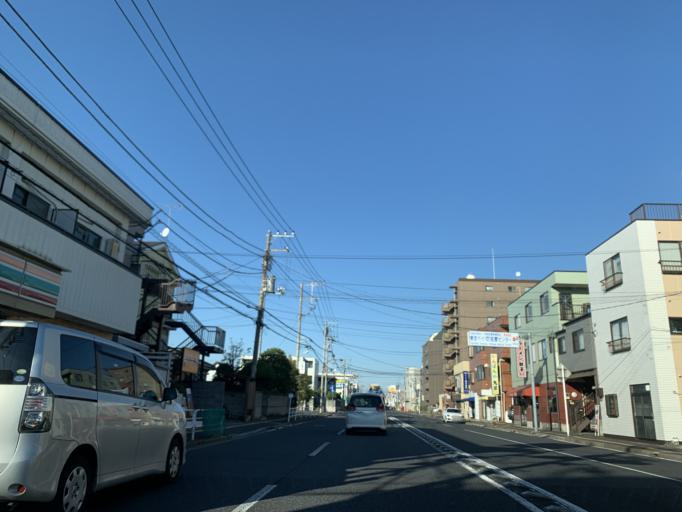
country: JP
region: Tokyo
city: Urayasu
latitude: 35.6708
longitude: 139.8946
